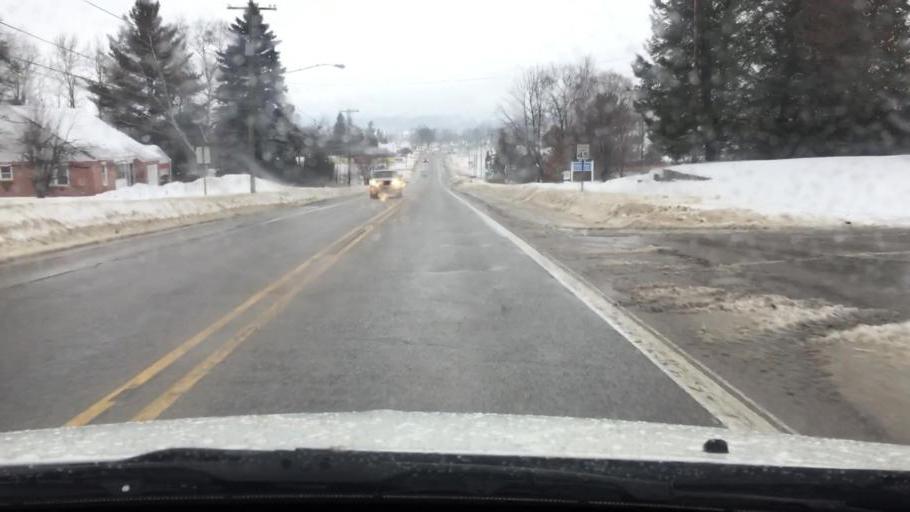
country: US
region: Michigan
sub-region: Charlevoix County
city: East Jordan
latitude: 45.1491
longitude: -85.1398
